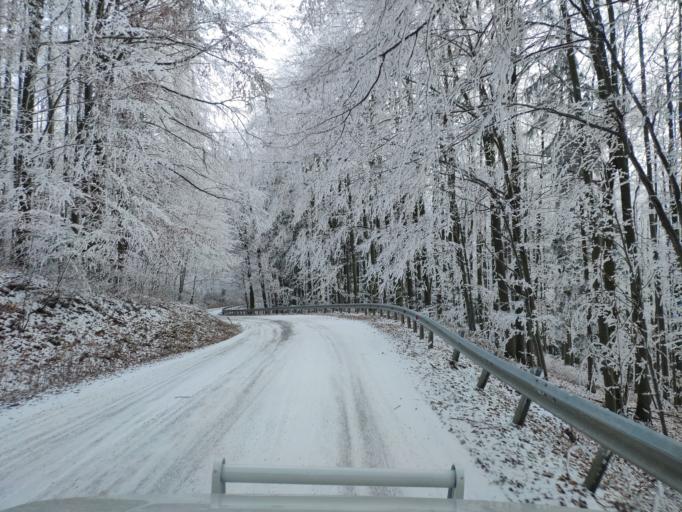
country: SK
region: Kosicky
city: Dobsina
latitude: 48.8063
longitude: 20.4846
